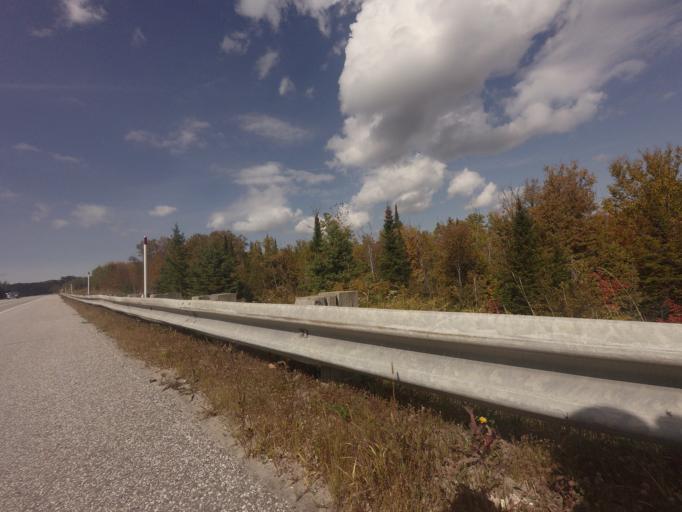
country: CA
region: Quebec
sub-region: Laurentides
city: Mont-Laurier
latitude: 46.5615
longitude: -75.6784
